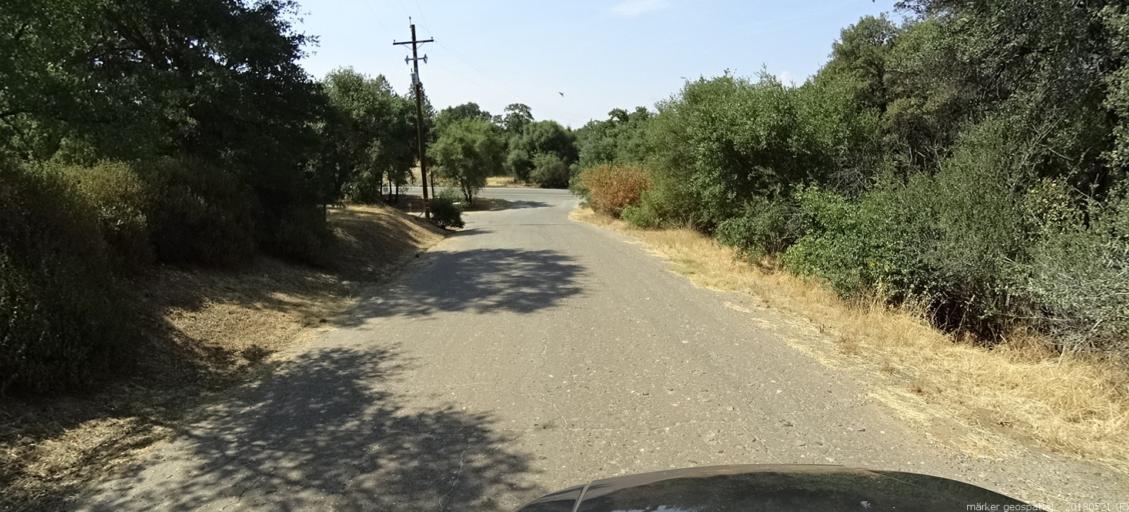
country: US
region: California
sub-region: Fresno County
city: Auberry
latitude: 37.2130
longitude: -119.5203
